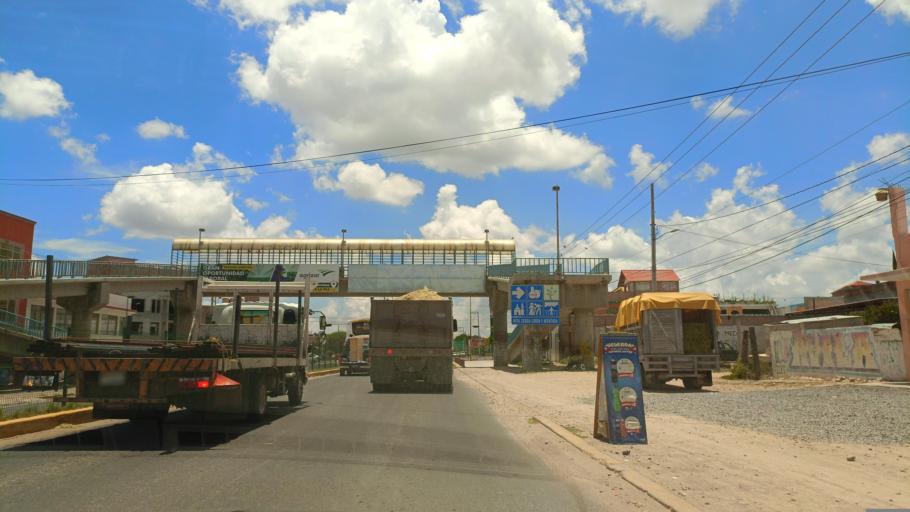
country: MX
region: Guerrero
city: San Luis de la Paz
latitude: 21.2886
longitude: -100.5114
